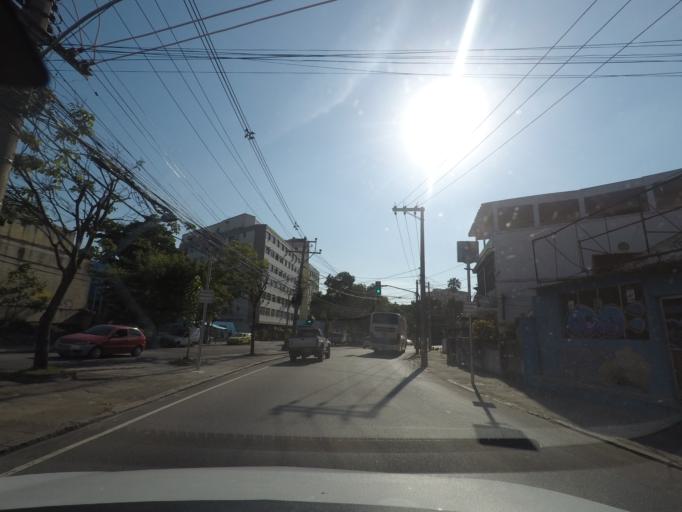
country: BR
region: Rio de Janeiro
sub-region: Duque De Caxias
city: Duque de Caxias
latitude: -22.8422
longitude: -43.2701
